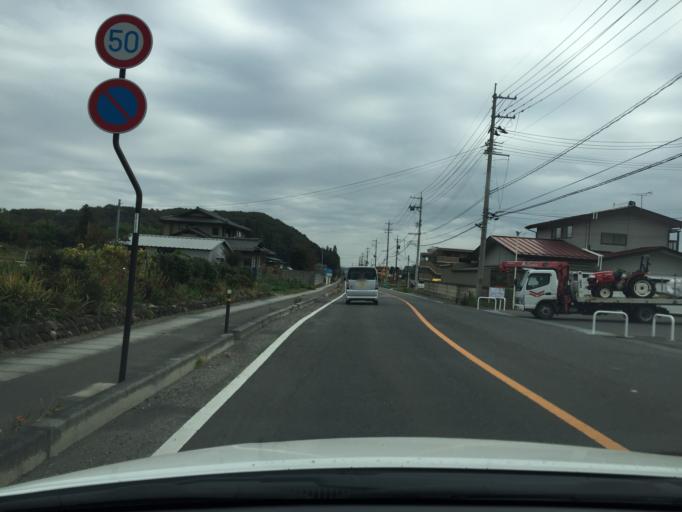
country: JP
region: Tochigi
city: Kuroiso
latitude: 37.1329
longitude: 140.1706
